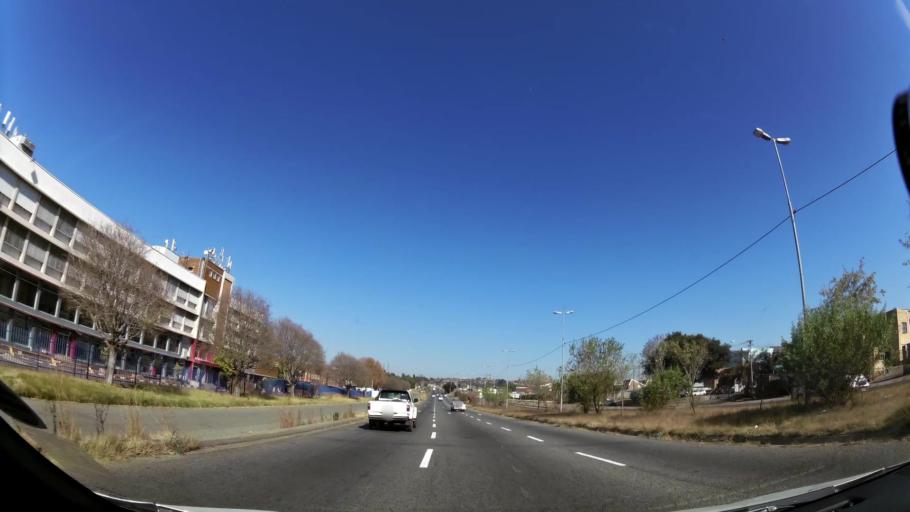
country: ZA
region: Gauteng
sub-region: Ekurhuleni Metropolitan Municipality
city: Germiston
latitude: -26.2487
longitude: 28.1042
